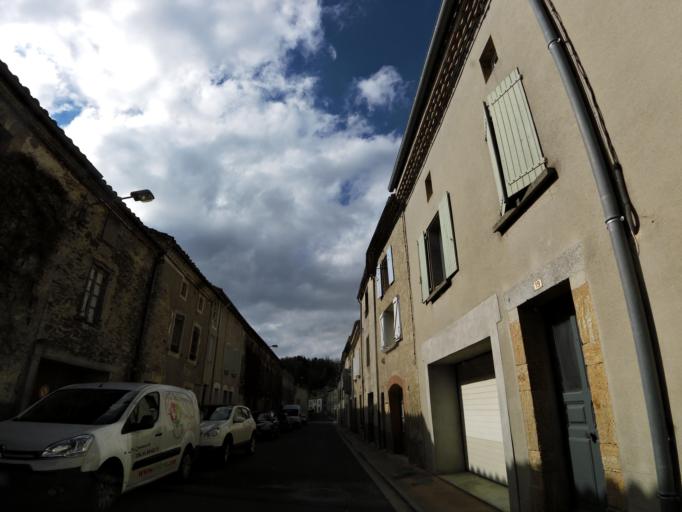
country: FR
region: Midi-Pyrenees
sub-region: Departement du Tarn
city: Soreze
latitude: 43.4110
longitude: 2.0794
